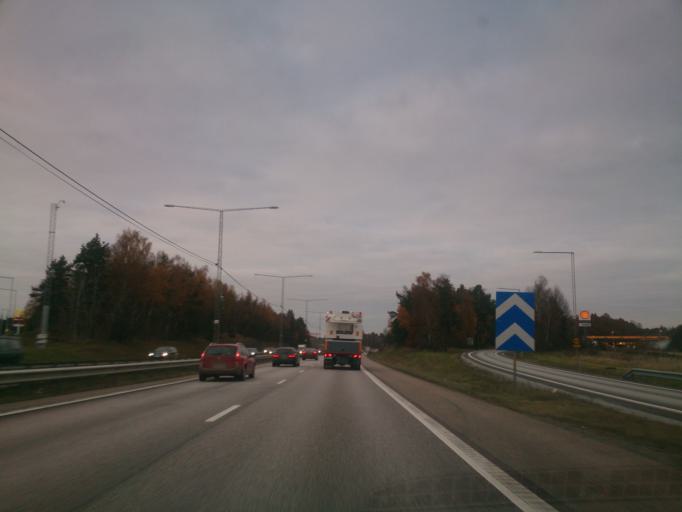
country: SE
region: Stockholm
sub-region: Upplands Vasby Kommun
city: Upplands Vaesby
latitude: 59.5484
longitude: 17.9005
